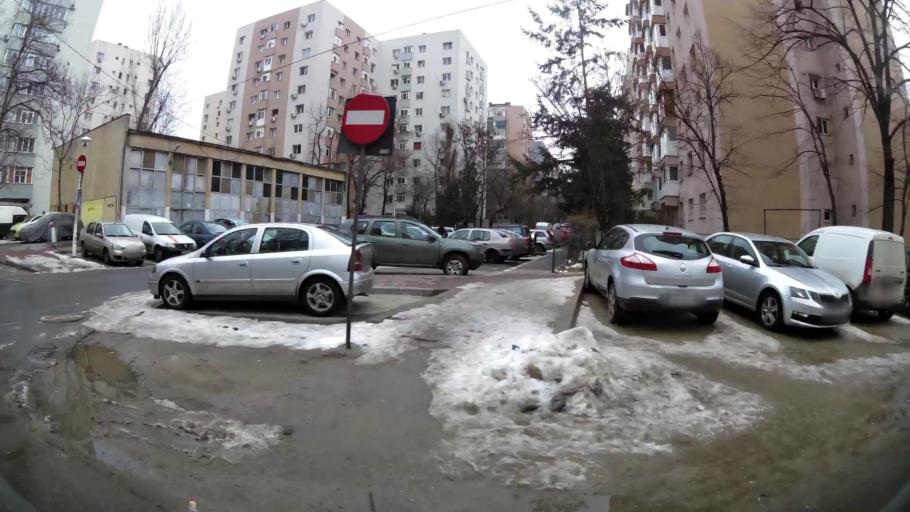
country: RO
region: Ilfov
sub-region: Comuna Popesti-Leordeni
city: Popesti-Leordeni
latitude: 44.4142
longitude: 26.1686
